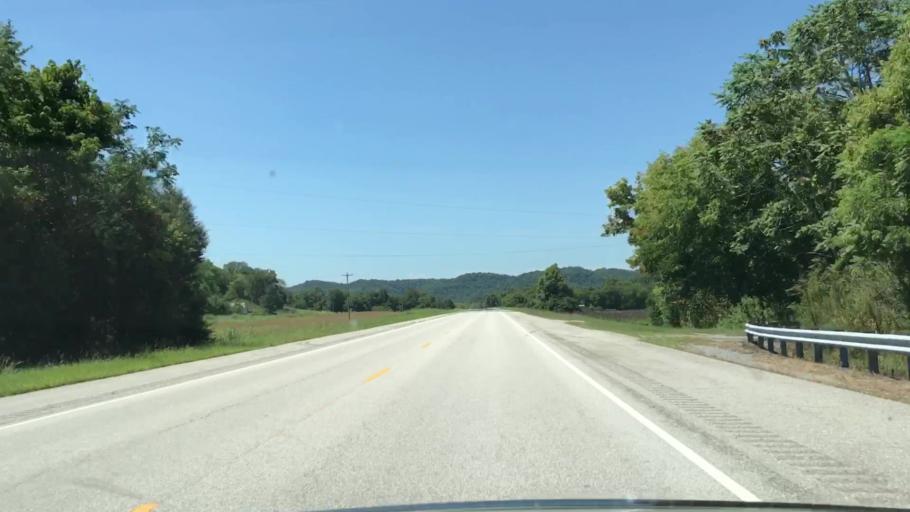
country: US
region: Tennessee
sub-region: Jackson County
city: Gainesboro
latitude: 36.4376
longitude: -85.6133
